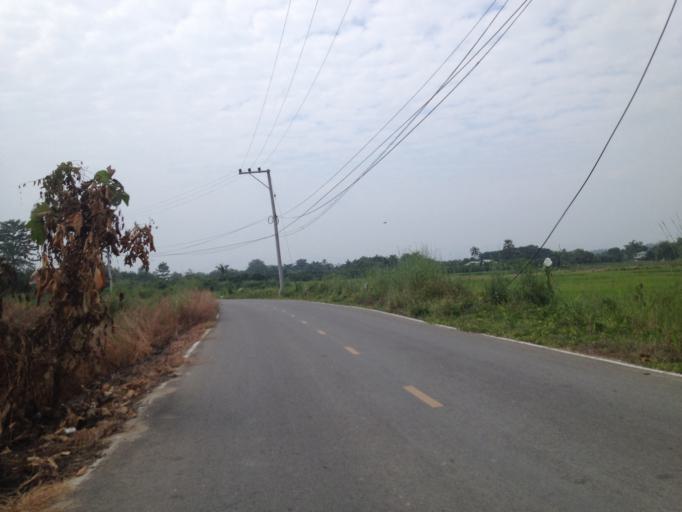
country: TH
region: Chiang Mai
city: San Pa Tong
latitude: 18.6590
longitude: 98.8776
